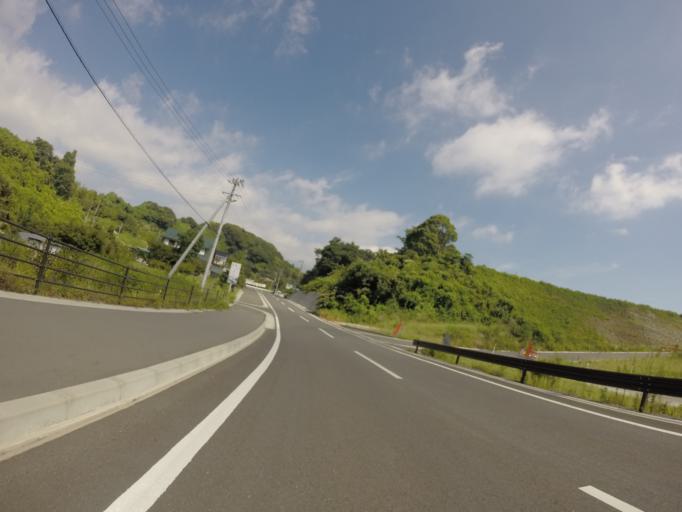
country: JP
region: Shizuoka
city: Shizuoka-shi
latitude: 34.9940
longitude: 138.4714
